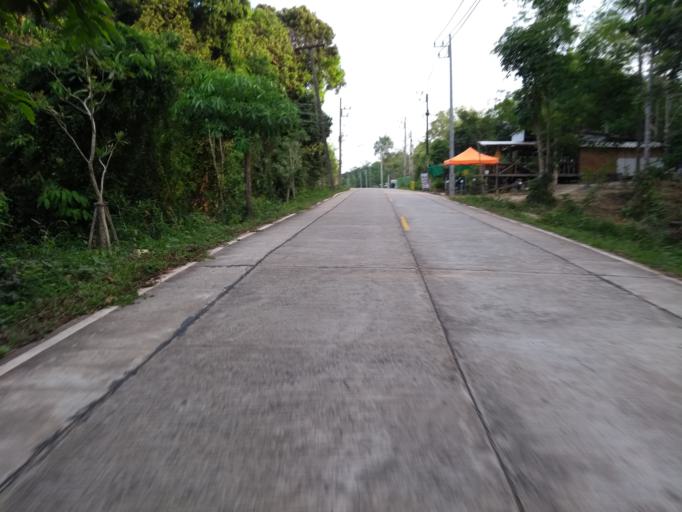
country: TH
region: Trat
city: Ko Kut
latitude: 11.6276
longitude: 102.5465
